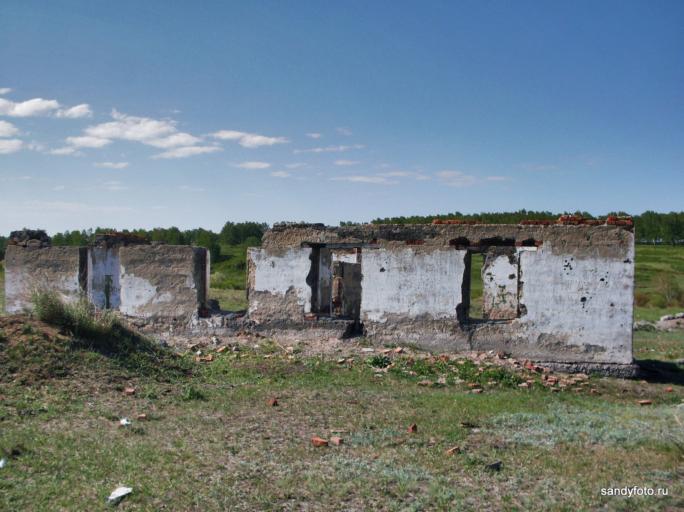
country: RU
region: Chelyabinsk
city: Troitsk
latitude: 54.1340
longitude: 61.4373
